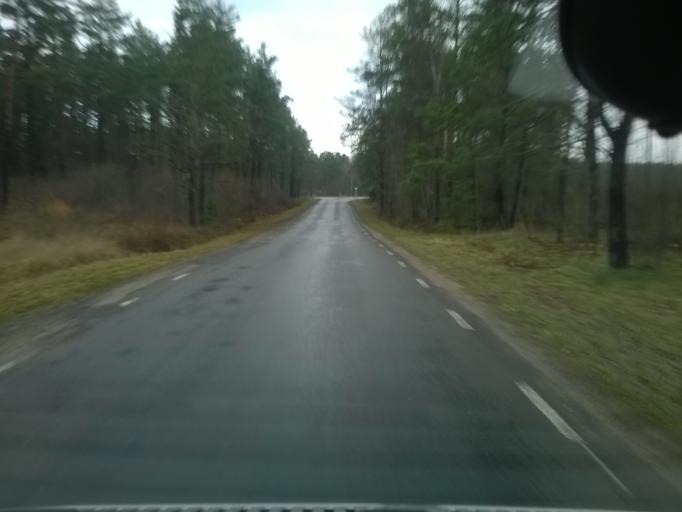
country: EE
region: Laeaene
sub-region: Ridala Parish
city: Uuemoisa
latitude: 58.9551
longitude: 23.7251
